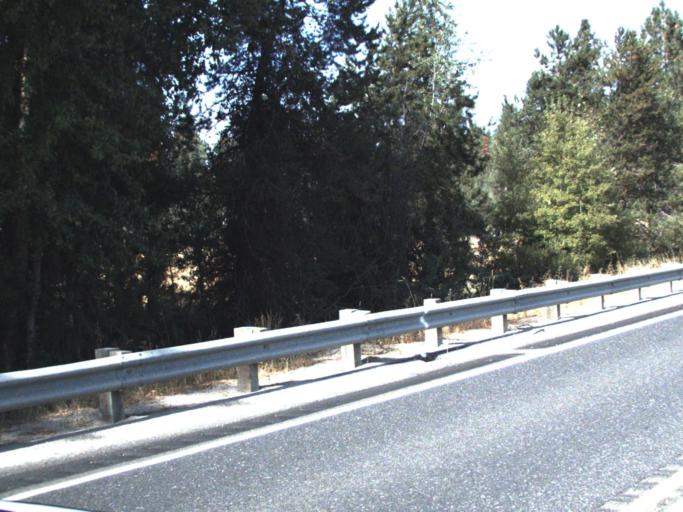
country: US
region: Washington
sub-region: Spokane County
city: Deer Park
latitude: 48.0182
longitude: -117.5891
